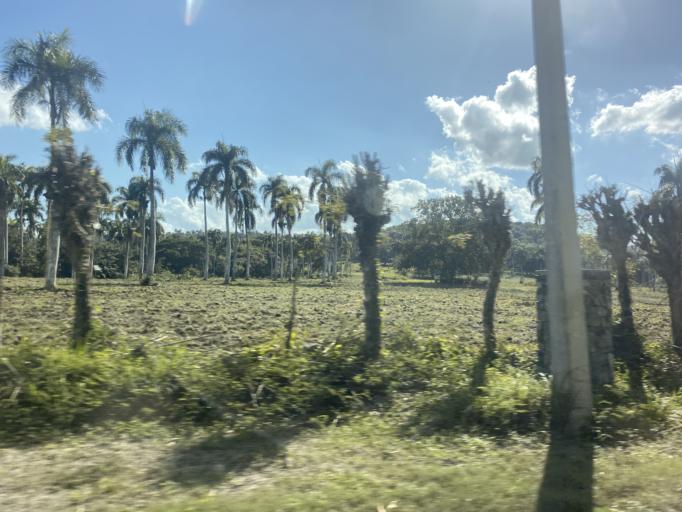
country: DO
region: Maria Trinidad Sanchez
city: Rio San Juan
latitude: 19.6153
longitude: -70.1323
